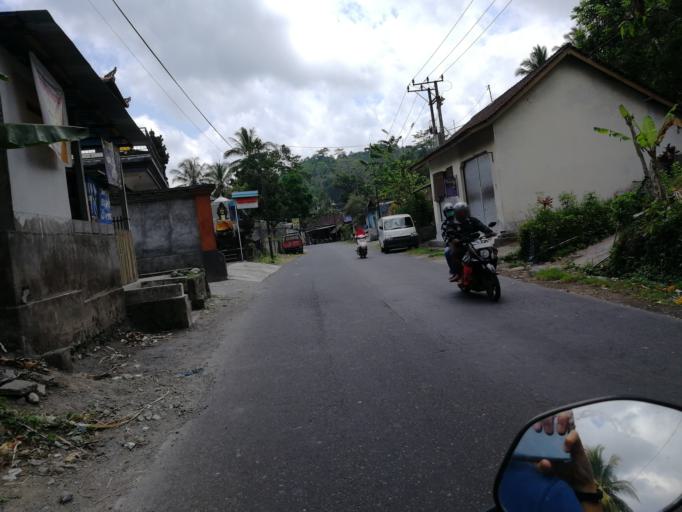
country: ID
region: Bali
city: Banjar Wangsian
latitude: -8.4590
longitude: 115.4493
